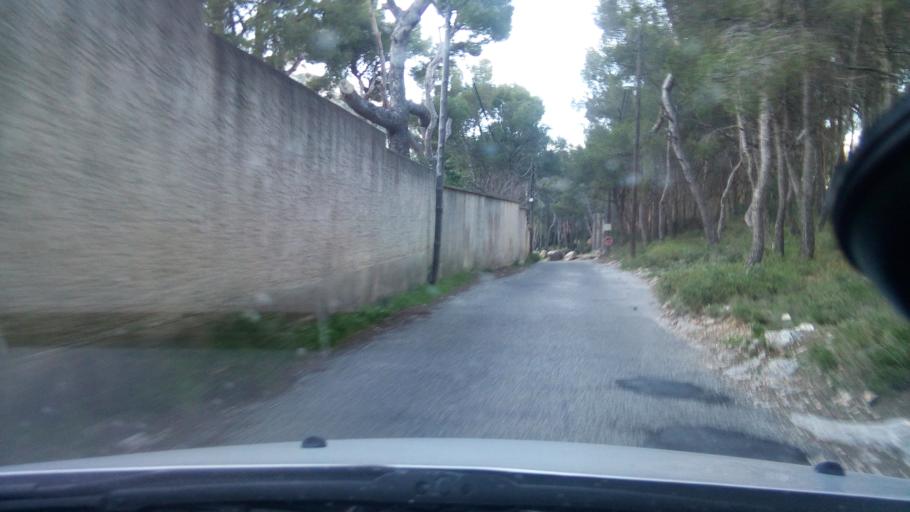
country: FR
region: Provence-Alpes-Cote d'Azur
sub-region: Departement des Bouches-du-Rhone
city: Marseille 09
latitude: 43.2221
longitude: 5.4066
